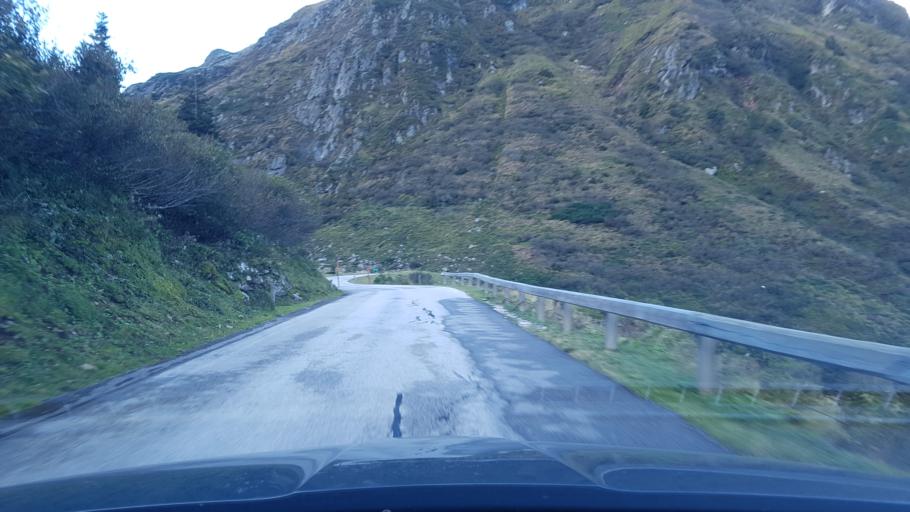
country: AT
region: Styria
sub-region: Politischer Bezirk Liezen
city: Sankt Nikolai im Solktal
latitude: 47.2755
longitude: 14.0819
